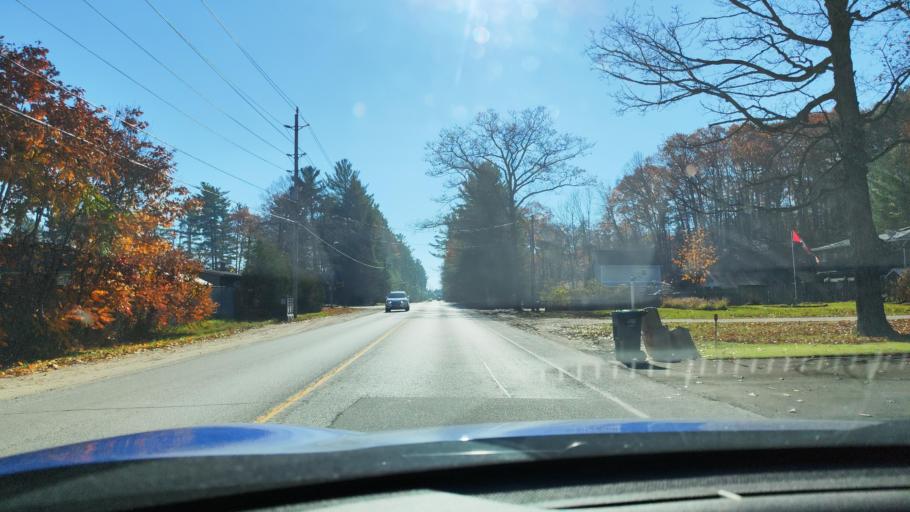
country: CA
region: Ontario
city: Wasaga Beach
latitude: 44.5177
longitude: -79.9950
